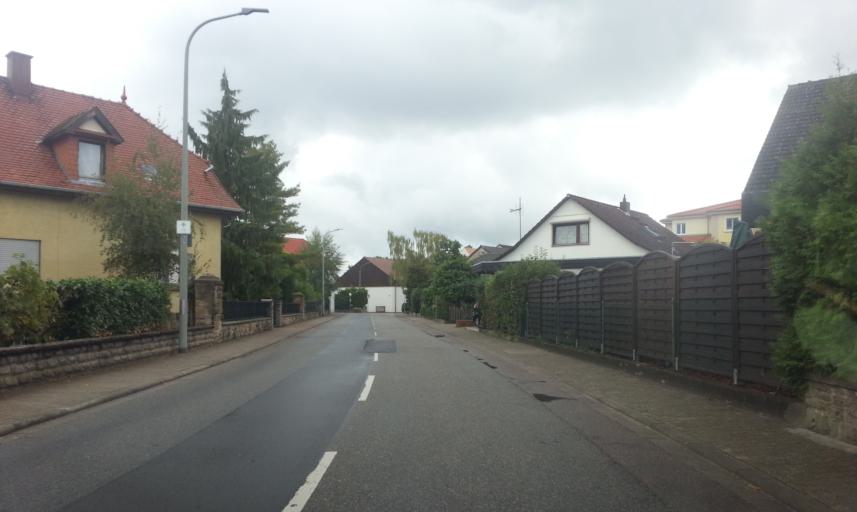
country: DE
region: Rheinland-Pfalz
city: Freinsheim
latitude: 49.5078
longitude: 8.2073
